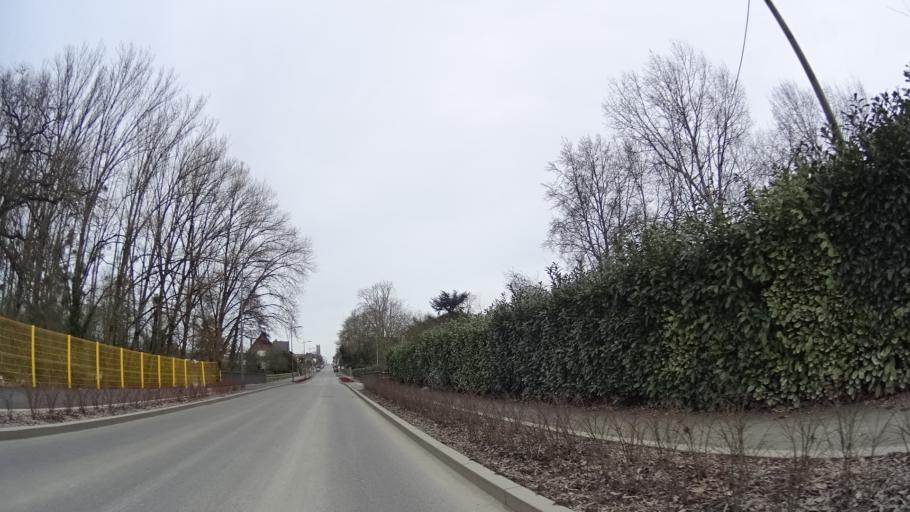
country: FR
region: Brittany
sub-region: Departement d'Ille-et-Vilaine
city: Montauban-de-Bretagne
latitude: 48.1927
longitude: -2.0504
